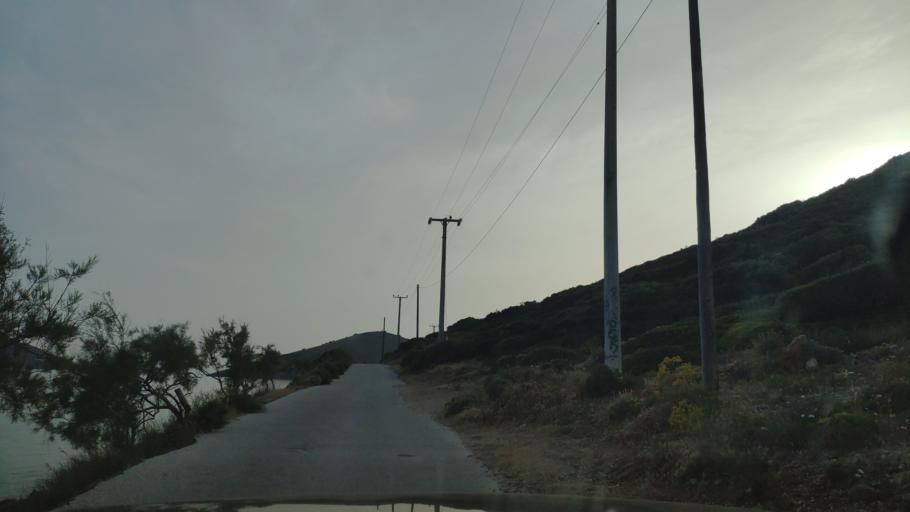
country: GR
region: Attica
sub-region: Nomarchia Anatolikis Attikis
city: Limin Mesoyaias
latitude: 37.8730
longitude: 24.0357
